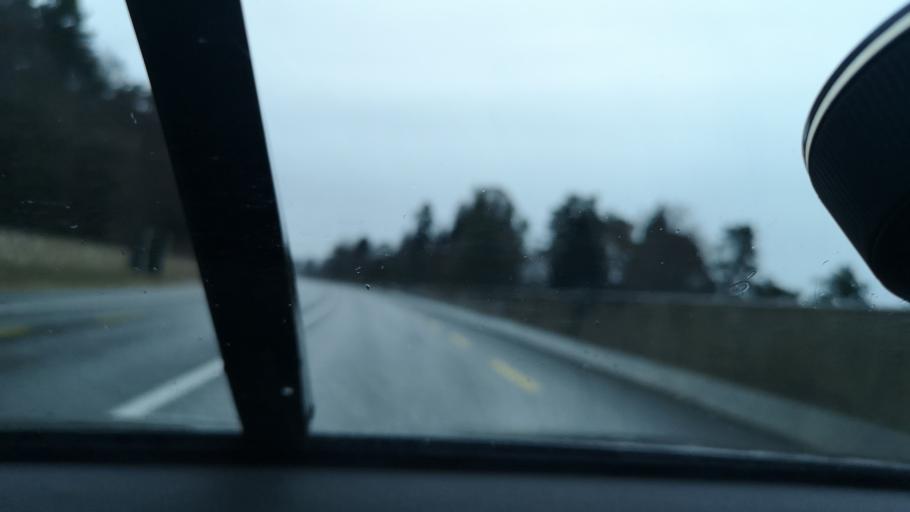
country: CH
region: Neuchatel
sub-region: Boudry District
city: Bevaix
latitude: 46.9168
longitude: 6.8049
